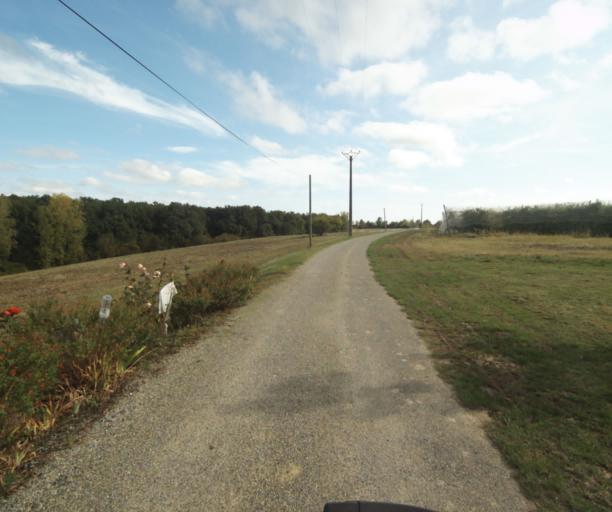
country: FR
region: Midi-Pyrenees
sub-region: Departement du Tarn-et-Garonne
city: Saint-Porquier
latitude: 43.9499
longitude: 1.1322
